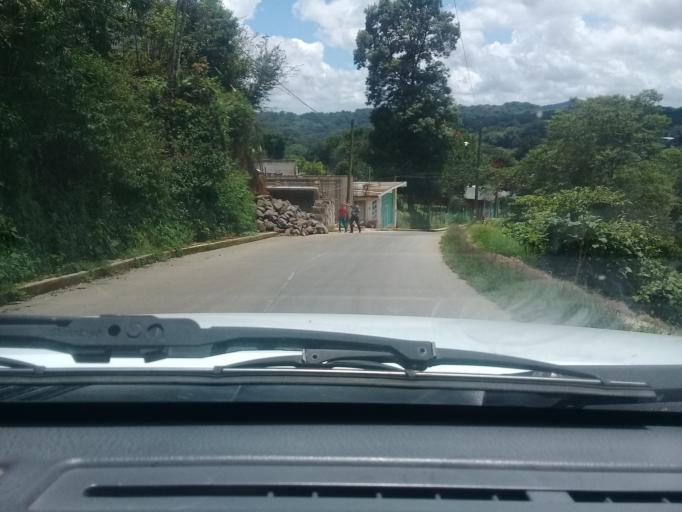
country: MX
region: Veracruz
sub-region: Tlalnelhuayocan
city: Otilpan
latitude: 19.5439
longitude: -96.9741
